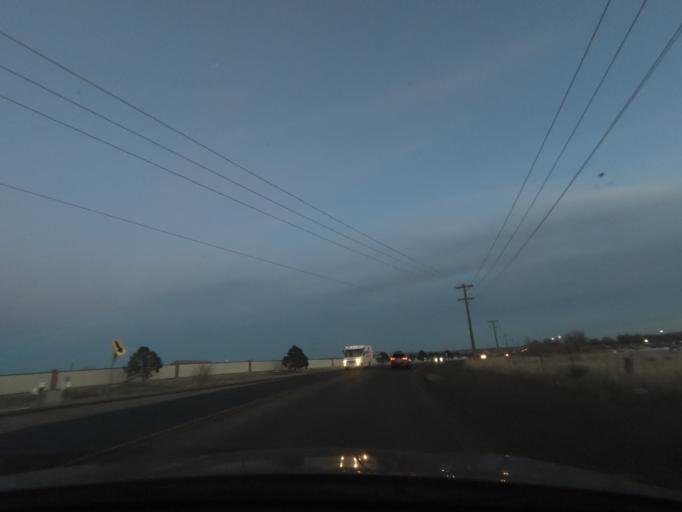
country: US
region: Colorado
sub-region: El Paso County
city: Stratmoor
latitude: 38.7770
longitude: -104.7709
